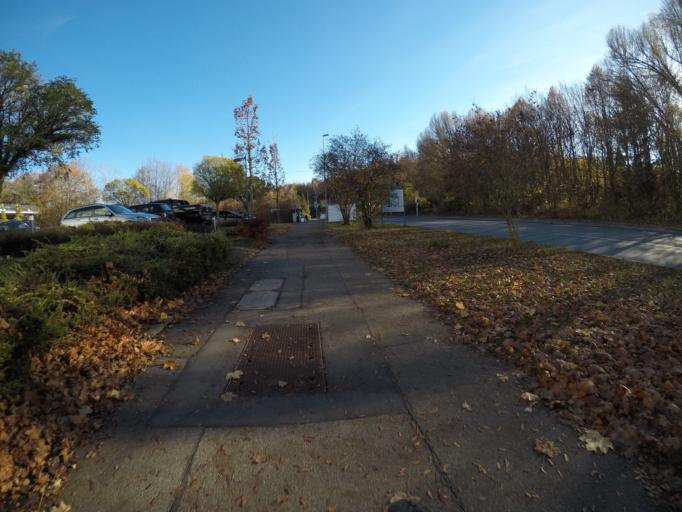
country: DE
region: Baden-Wuerttemberg
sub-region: Regierungsbezirk Stuttgart
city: Ehningen
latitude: 48.6771
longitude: 8.9712
